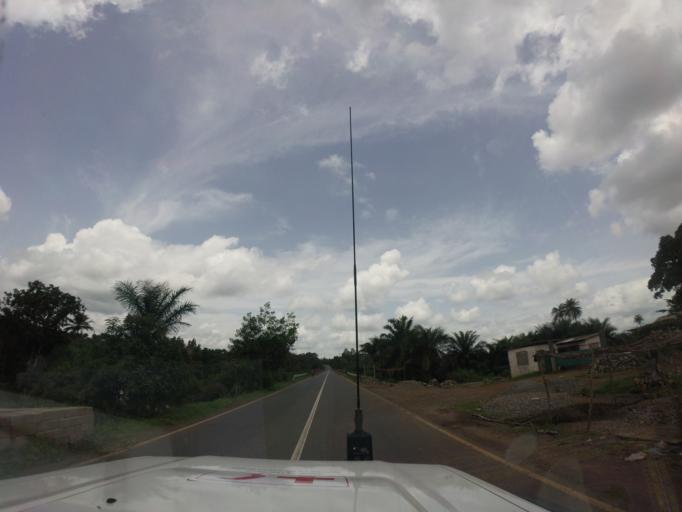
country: SL
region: Northern Province
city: Mange
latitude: 8.9258
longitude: -12.8504
